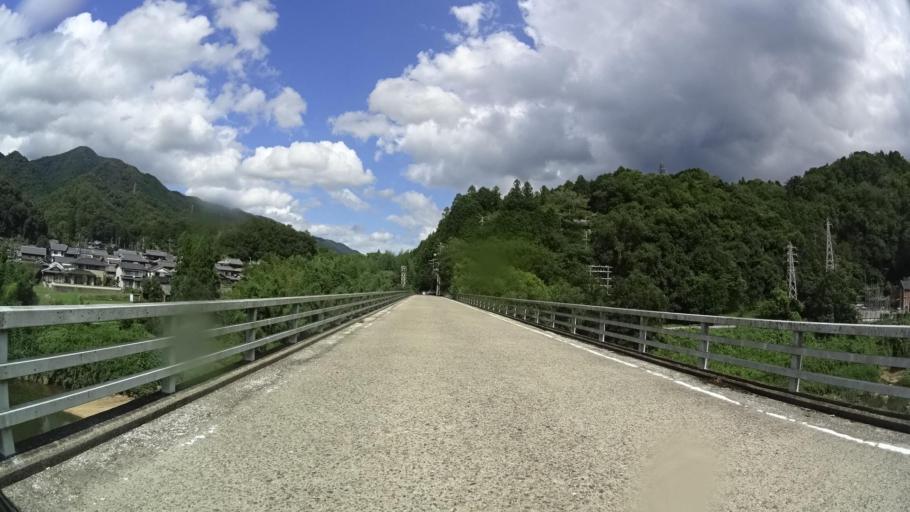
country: JP
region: Mie
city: Ueno-ebisumachi
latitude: 34.7696
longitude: 135.9974
